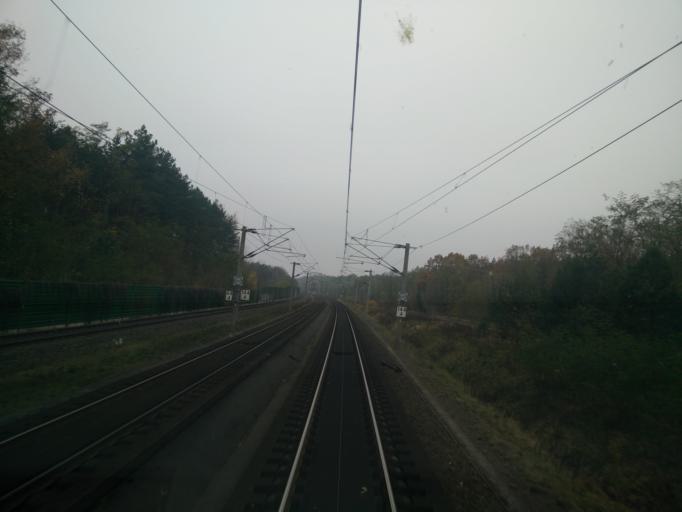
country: DE
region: Brandenburg
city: Retzow
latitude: 52.5885
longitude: 12.7445
